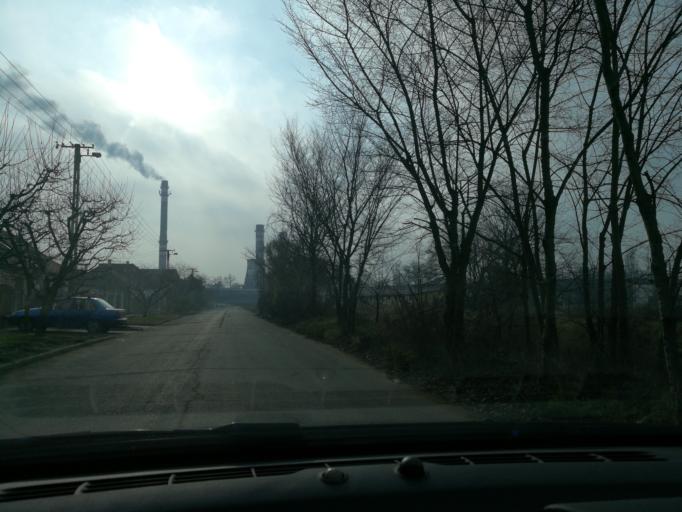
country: HU
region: Szabolcs-Szatmar-Bereg
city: Nyiregyhaza
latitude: 47.9598
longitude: 21.6988
